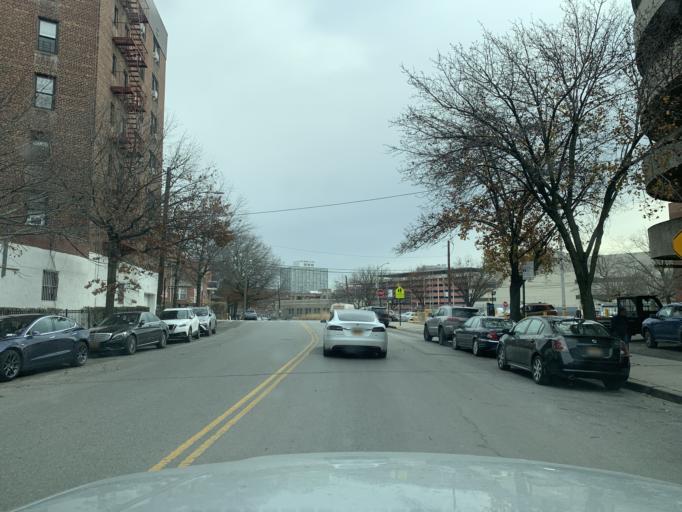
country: US
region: New York
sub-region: Queens County
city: Borough of Queens
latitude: 40.7362
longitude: -73.8736
